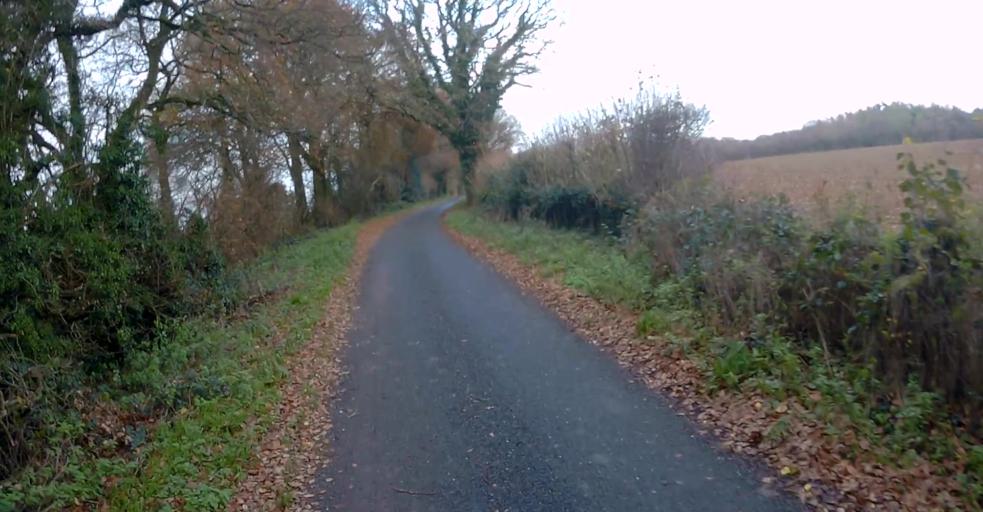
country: GB
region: England
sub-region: Hampshire
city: Basingstoke
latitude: 51.1837
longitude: -1.0982
